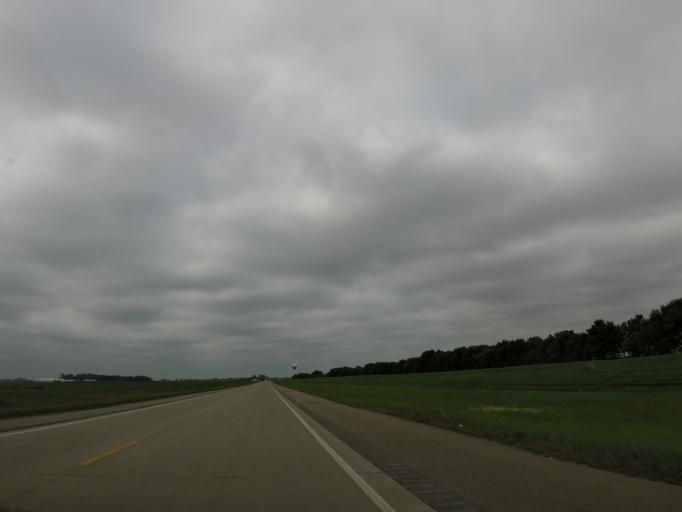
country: US
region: Minnesota
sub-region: Renville County
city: Renville
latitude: 44.7893
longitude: -95.1630
